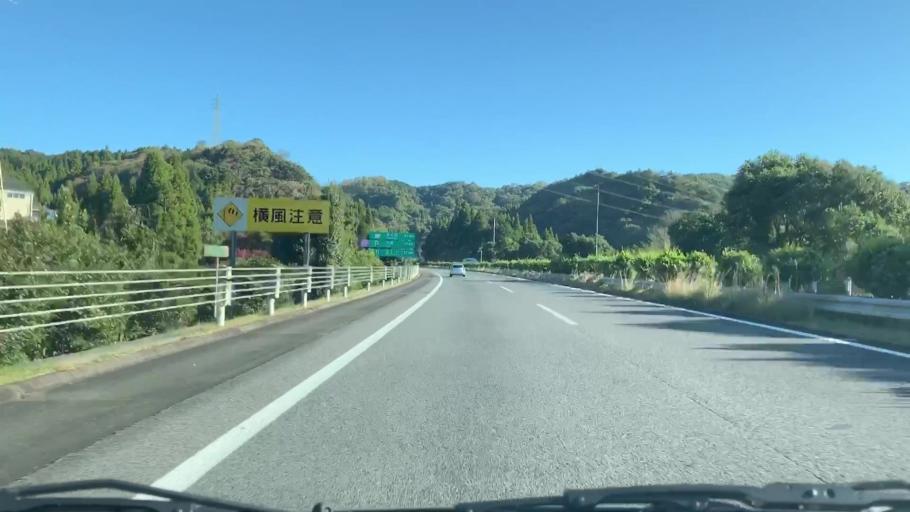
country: JP
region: Saga Prefecture
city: Takeocho-takeo
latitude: 33.2356
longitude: 130.0610
